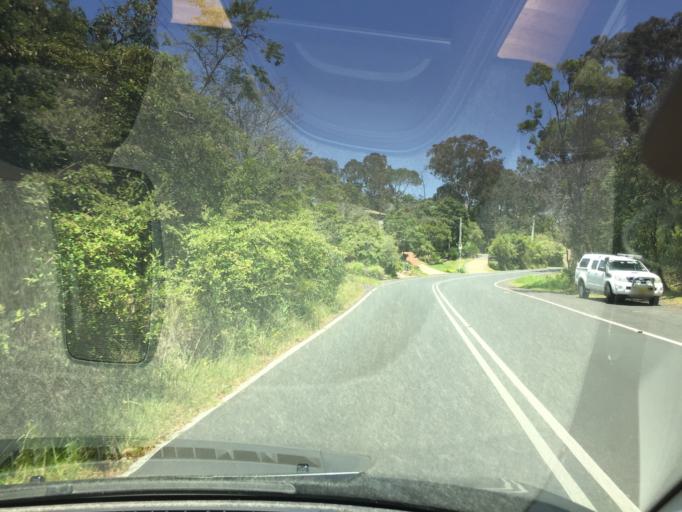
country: AU
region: New South Wales
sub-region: Bega Valley
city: Merimbula
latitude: -36.8893
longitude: 149.9248
